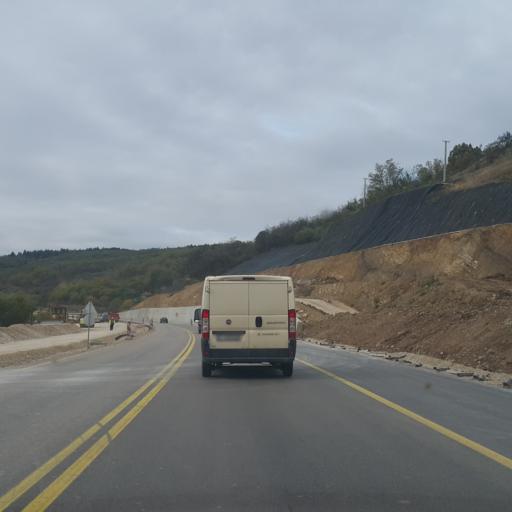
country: RS
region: Central Serbia
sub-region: Pirotski Okrug
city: Bela Palanka
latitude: 43.2318
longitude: 22.4582
